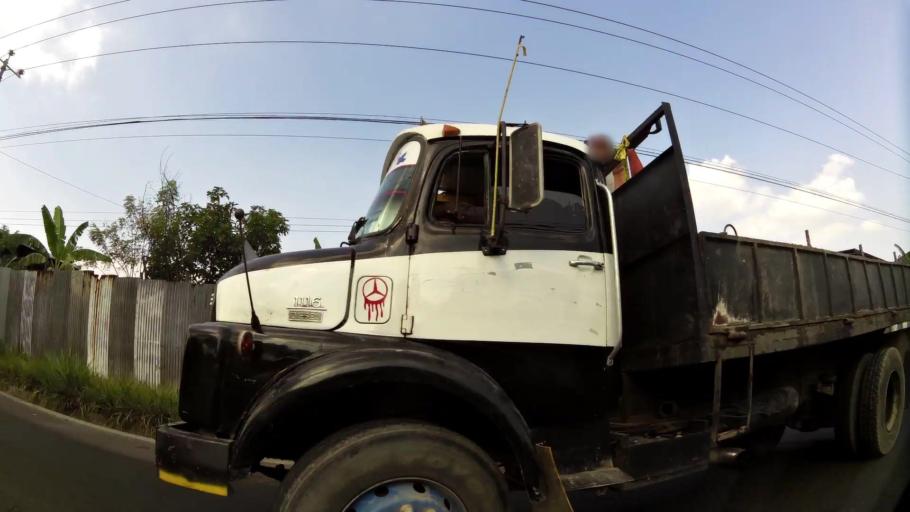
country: SV
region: San Salvador
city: Soyapango
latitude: 13.7173
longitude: -89.1420
